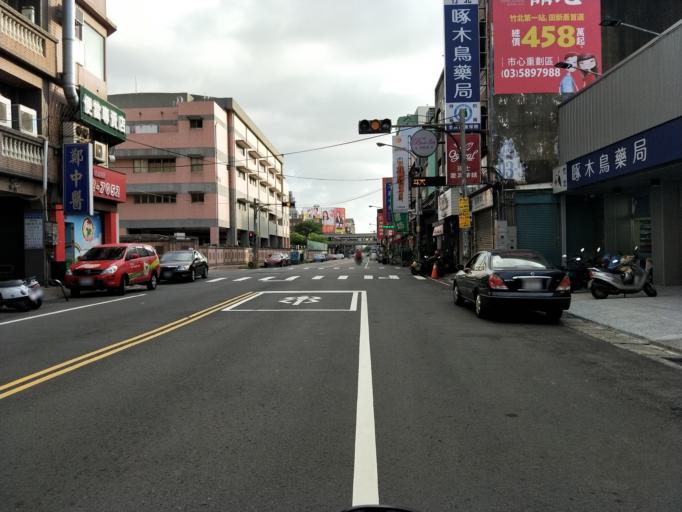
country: TW
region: Taiwan
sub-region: Hsinchu
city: Zhubei
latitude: 24.8322
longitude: 121.0055
